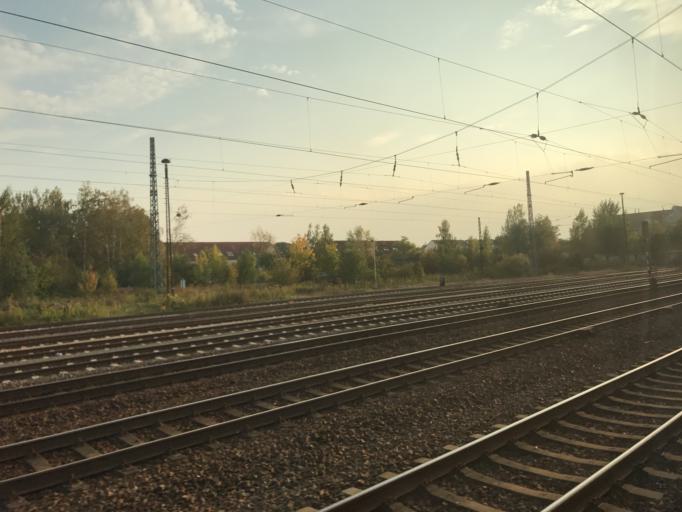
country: DE
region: Saxony
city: Leipzig
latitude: 51.3883
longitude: 12.3627
